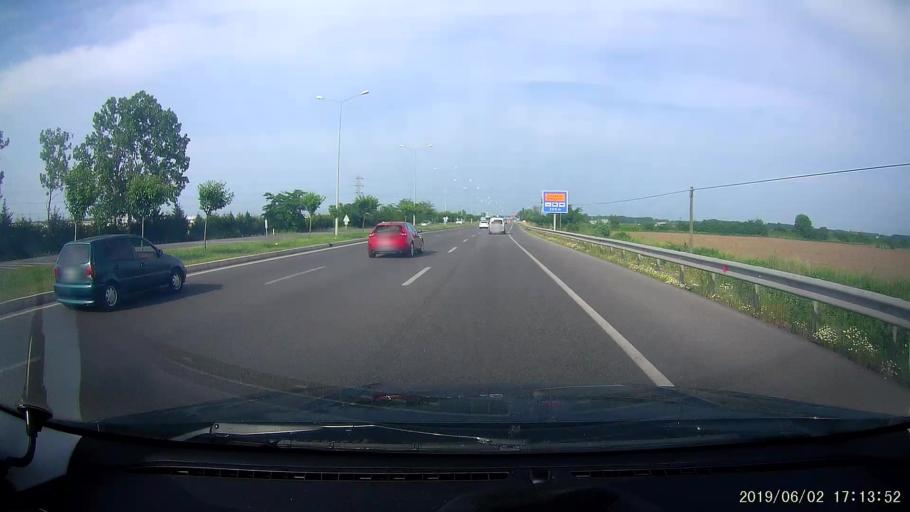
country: TR
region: Samsun
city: Tekkekoy
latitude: 41.2328
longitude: 36.5180
